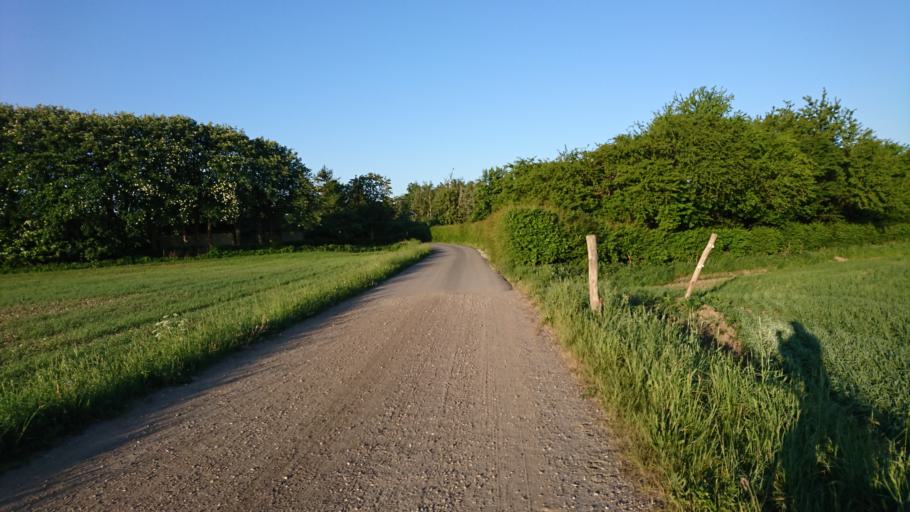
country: DK
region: Capital Region
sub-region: Egedal Kommune
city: Smorumnedre
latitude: 55.7327
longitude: 12.3185
